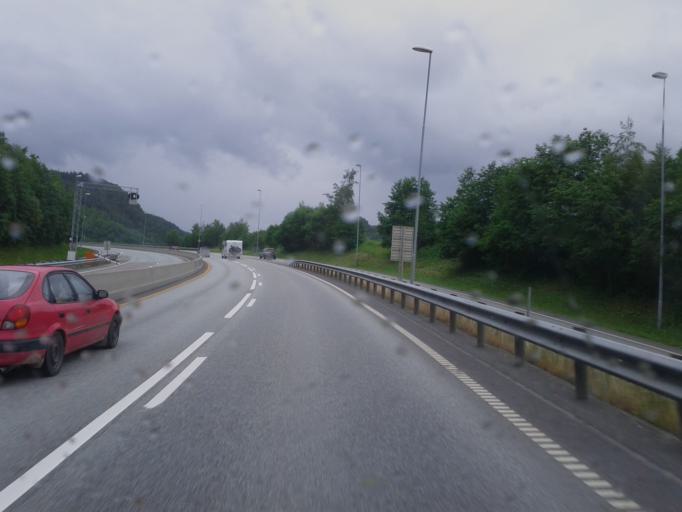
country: NO
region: Sor-Trondelag
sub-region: Malvik
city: Hommelvik
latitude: 63.4117
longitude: 10.8175
